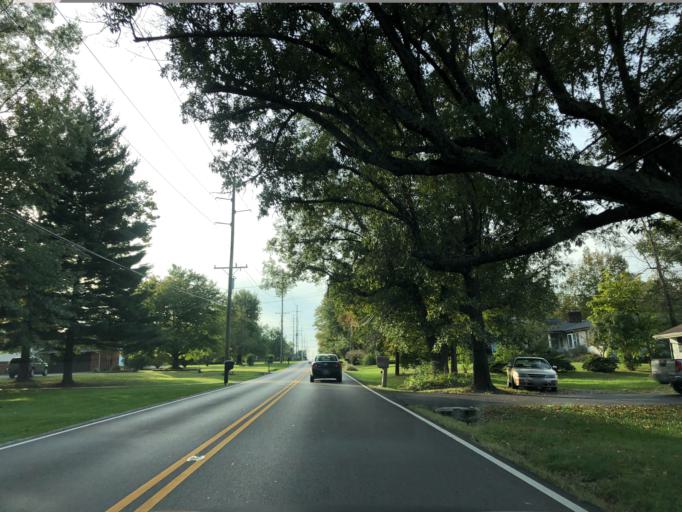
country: US
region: Ohio
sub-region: Warren County
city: Loveland Park
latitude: 39.2894
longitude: -84.2783
